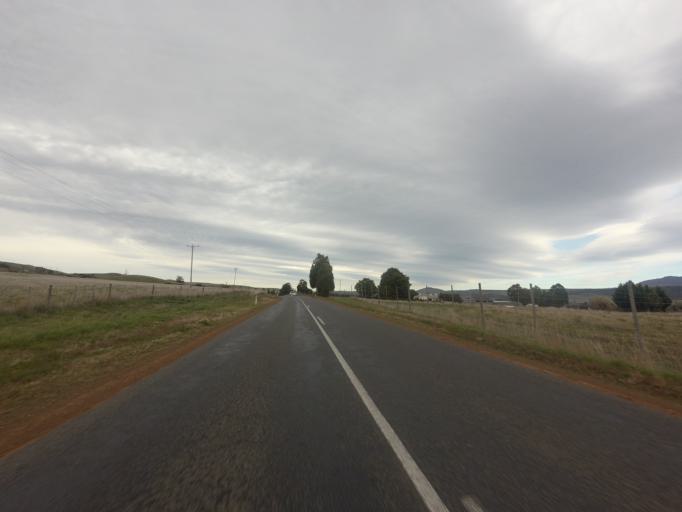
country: AU
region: Tasmania
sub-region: Derwent Valley
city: New Norfolk
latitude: -42.5128
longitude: 146.7429
